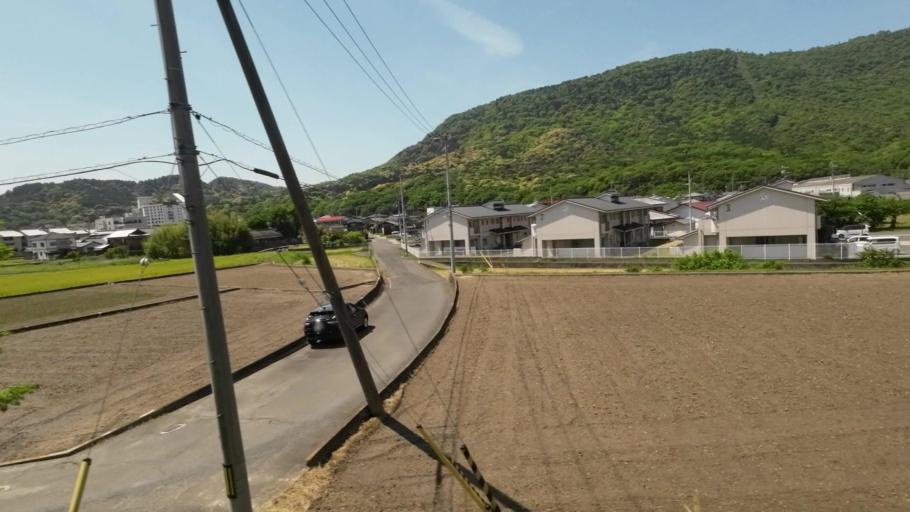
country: JP
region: Kagawa
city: Marugame
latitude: 34.1974
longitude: 133.8158
